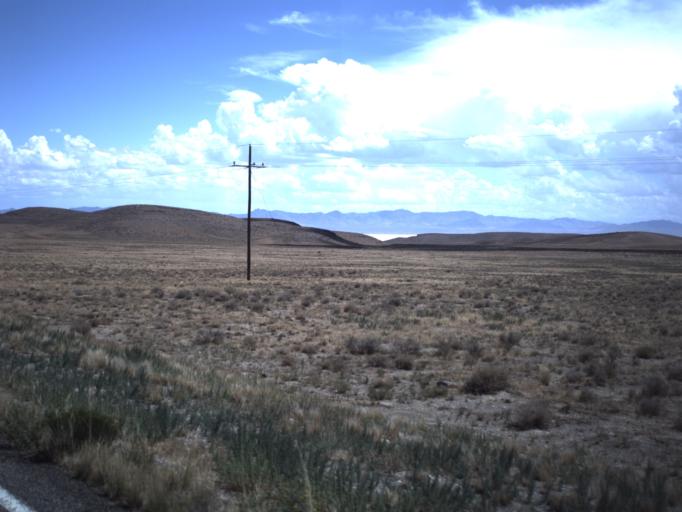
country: US
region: Utah
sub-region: Beaver County
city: Milford
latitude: 39.0388
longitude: -113.3087
